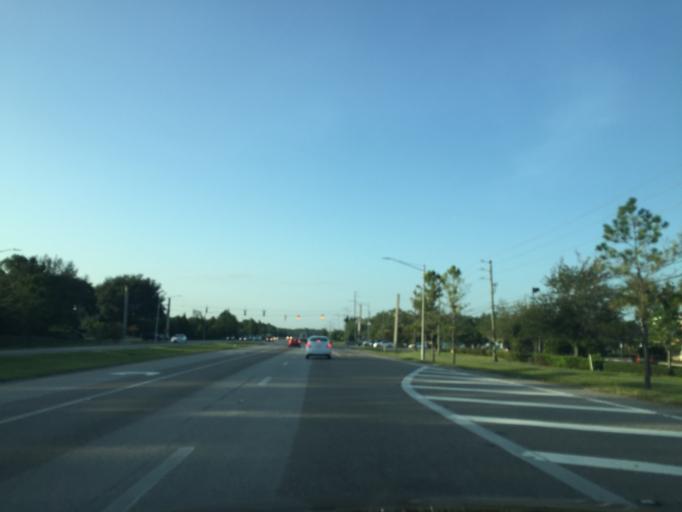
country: US
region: Florida
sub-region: Orange County
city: Alafaya
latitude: 28.5365
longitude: -81.2078
